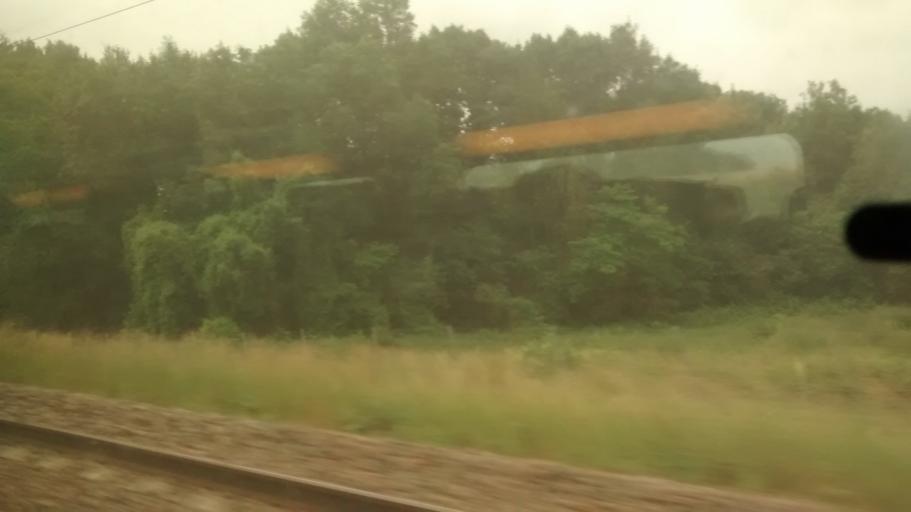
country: FR
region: Ile-de-France
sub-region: Departement de Seine-et-Marne
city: Moisenay
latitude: 48.5534
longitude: 2.7727
